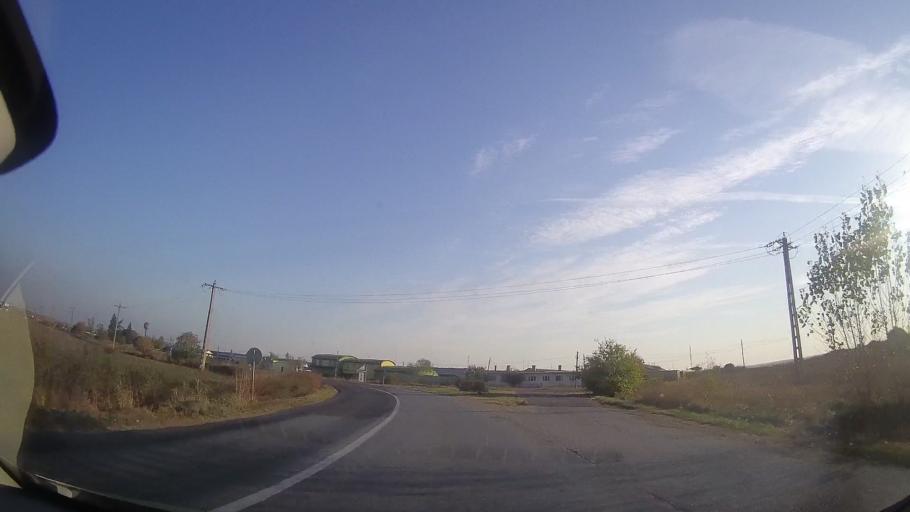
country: RO
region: Timis
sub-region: Comuna Pischia
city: Pischia
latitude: 45.8882
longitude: 21.3485
